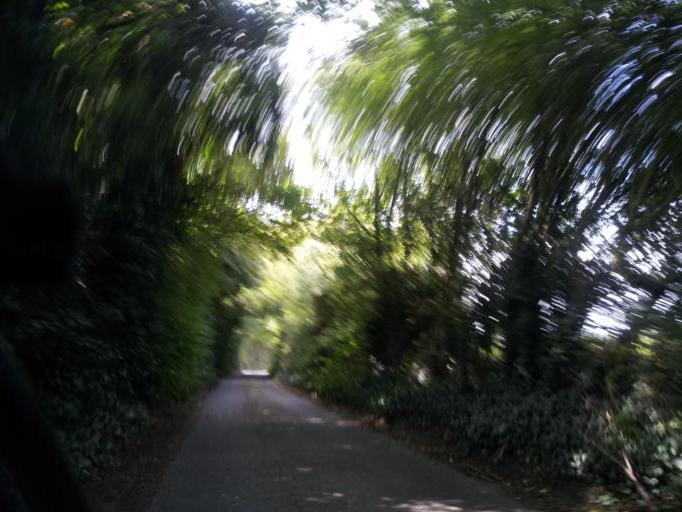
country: GB
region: England
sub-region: Kent
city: Rainham
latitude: 51.3479
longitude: 0.6160
